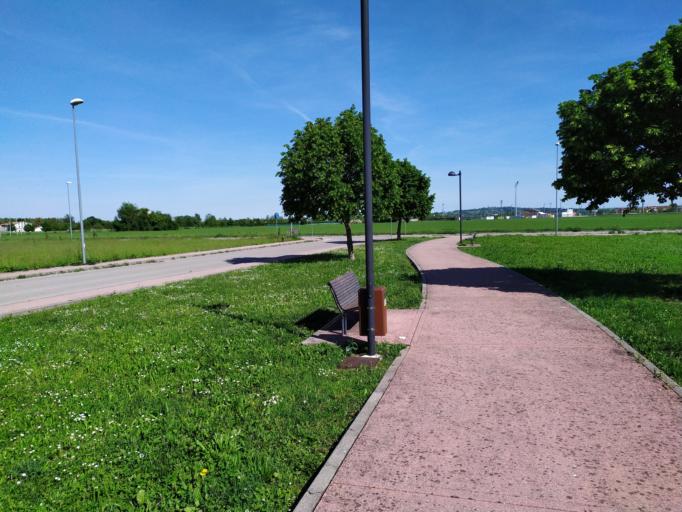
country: IT
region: Veneto
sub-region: Provincia di Vicenza
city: Thiene
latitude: 45.7005
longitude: 11.4924
